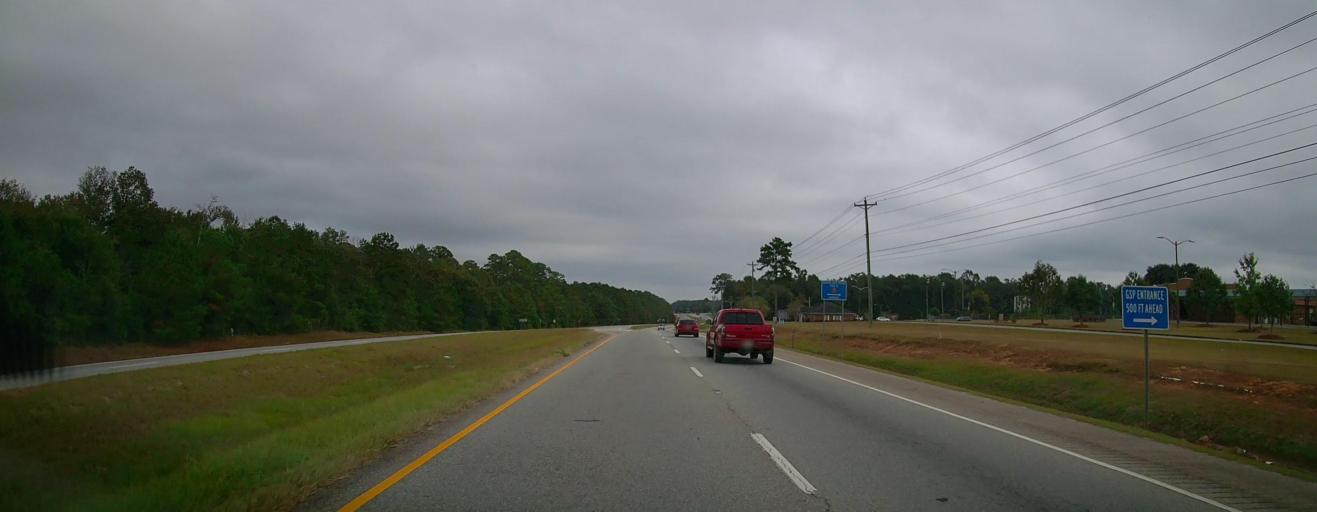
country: US
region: Georgia
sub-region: Thomas County
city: Thomasville
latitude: 30.8747
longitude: -83.9666
